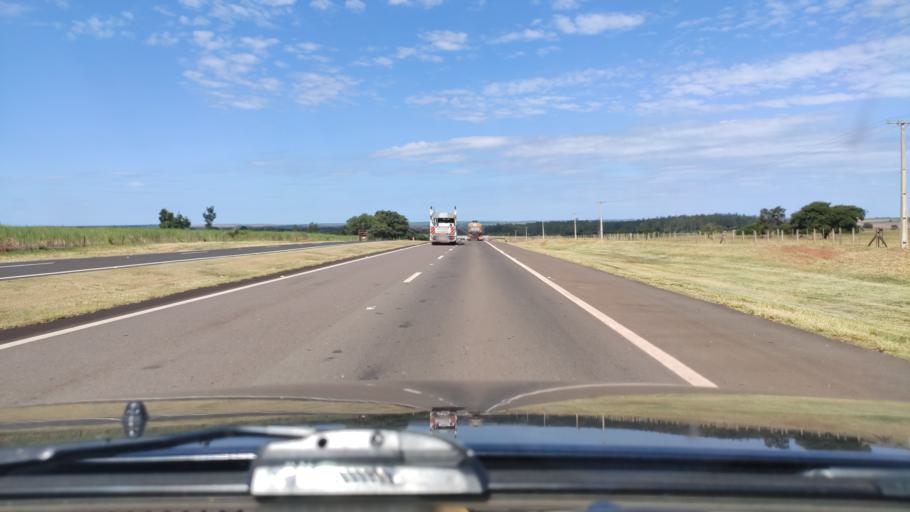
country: BR
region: Sao Paulo
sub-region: Rancharia
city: Rancharia
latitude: -22.4580
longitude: -50.9697
